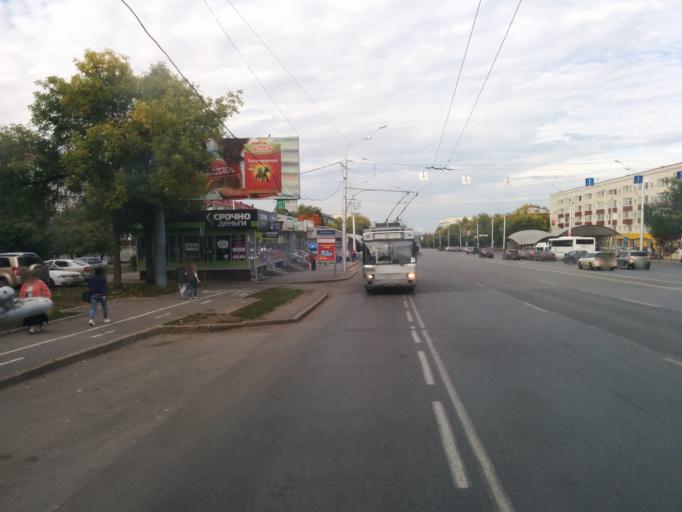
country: RU
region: Bashkortostan
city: Ufa
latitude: 54.7890
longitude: 56.0354
